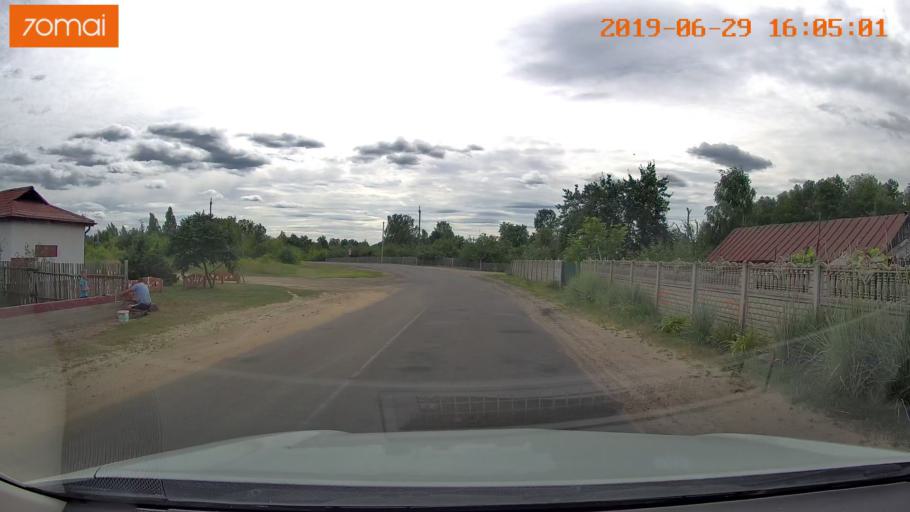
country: BY
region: Brest
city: Luninyets
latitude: 52.2187
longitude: 27.0220
